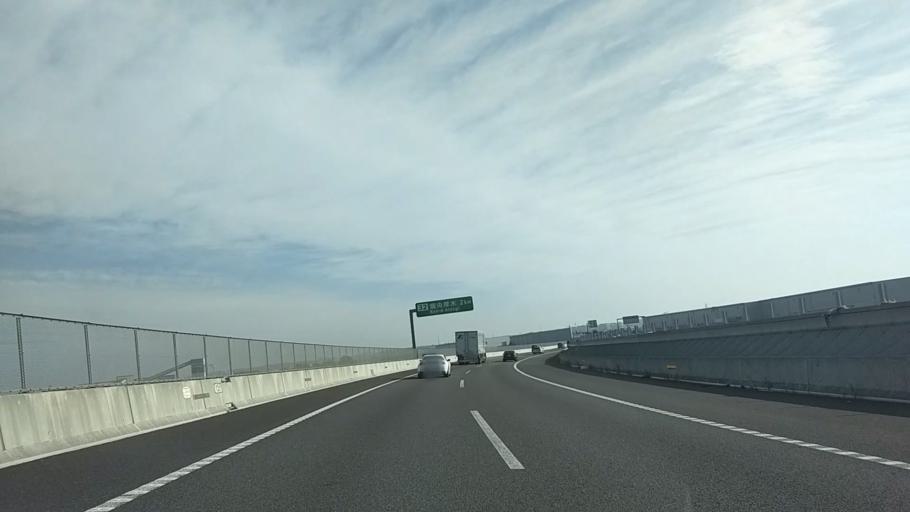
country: JP
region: Kanagawa
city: Atsugi
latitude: 35.4599
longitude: 139.3725
